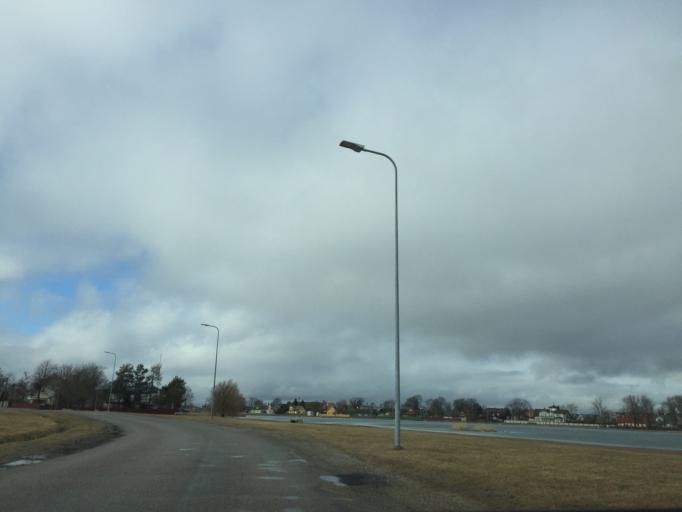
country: EE
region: Laeaene
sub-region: Haapsalu linn
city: Haapsalu
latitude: 58.9512
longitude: 23.5265
